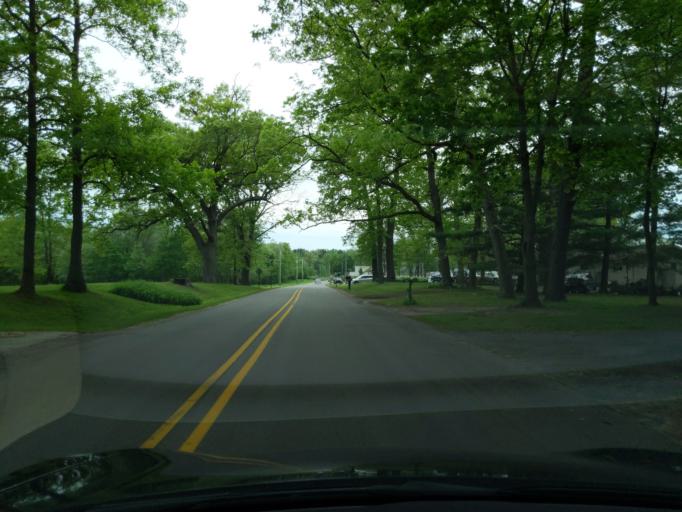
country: US
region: Michigan
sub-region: Ingham County
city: Leslie
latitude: 42.3887
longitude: -84.3509
